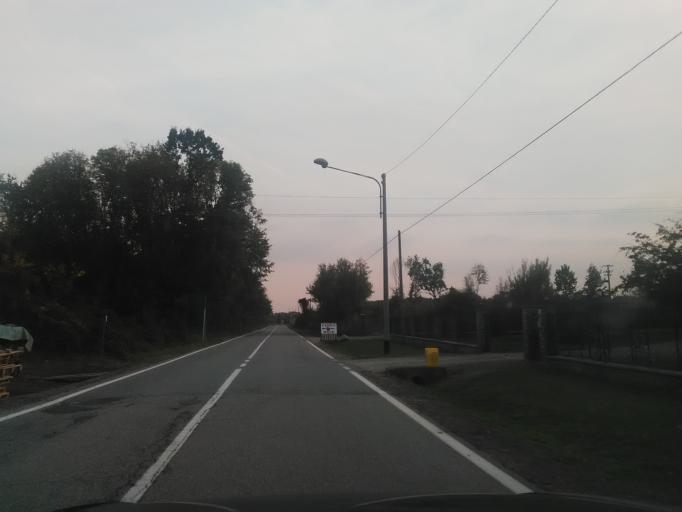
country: IT
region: Piedmont
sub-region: Provincia di Vercelli
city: San Maurizio
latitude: 45.5980
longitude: 8.2920
